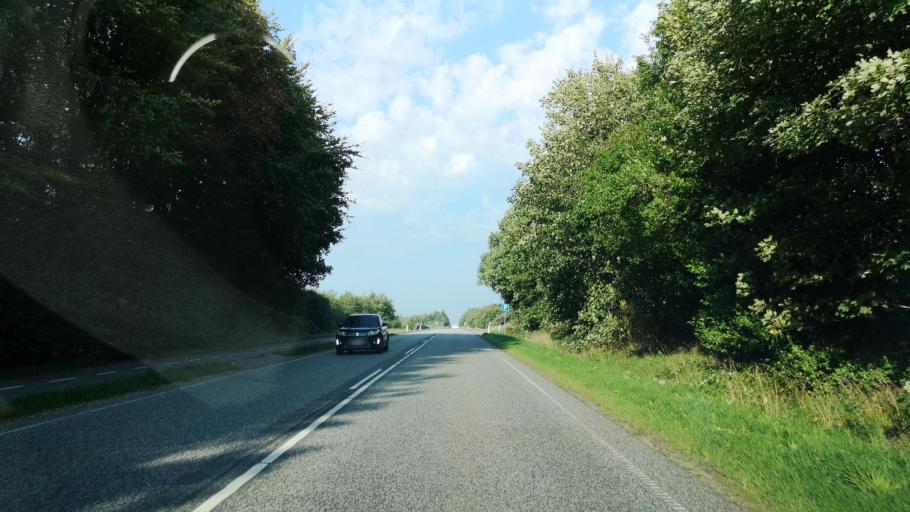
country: DK
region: Central Jutland
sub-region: Herning Kommune
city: Kibaek
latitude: 56.0489
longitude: 8.8824
